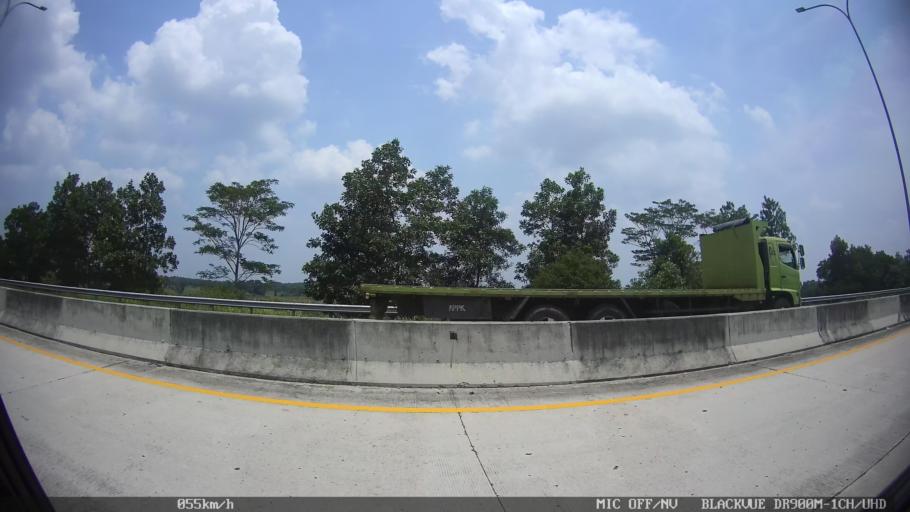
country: ID
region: Lampung
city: Natar
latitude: -5.2749
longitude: 105.2130
